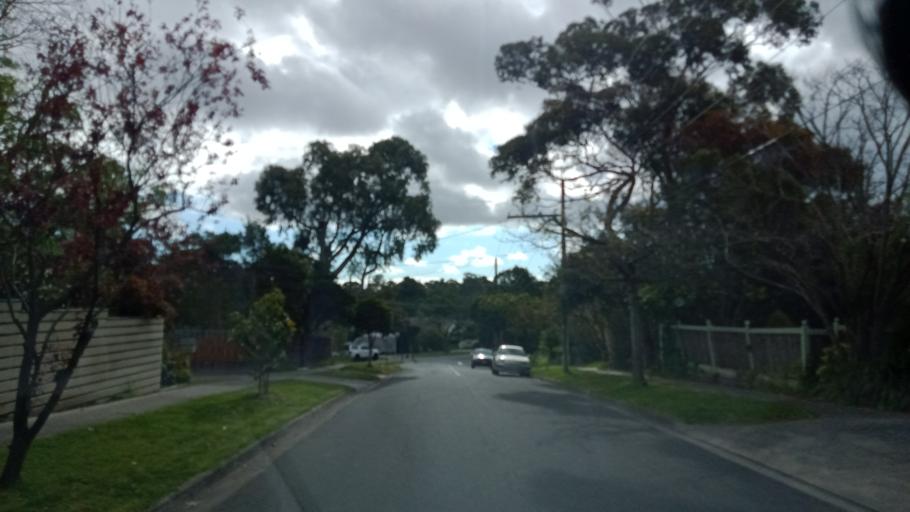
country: AU
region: Victoria
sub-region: Monash
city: Notting Hill
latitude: -37.8840
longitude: 145.1507
